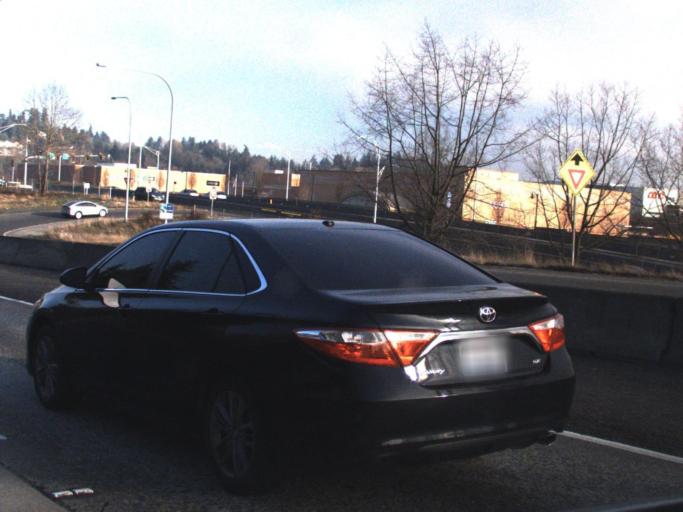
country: US
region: Washington
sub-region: King County
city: Tukwila
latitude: 47.4563
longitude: -122.2635
